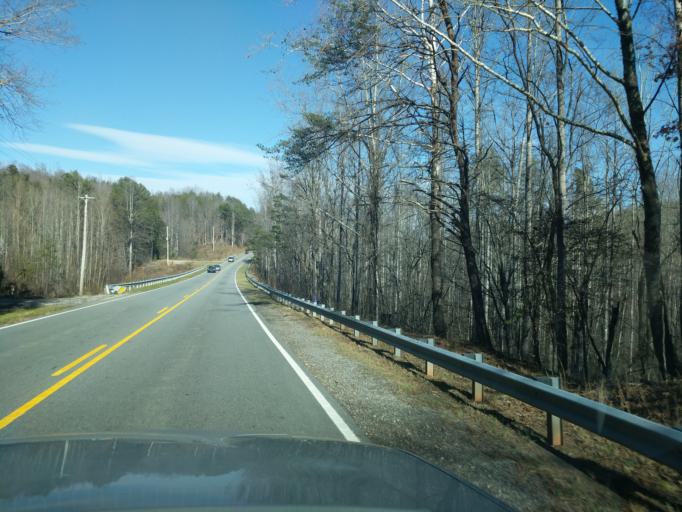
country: US
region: North Carolina
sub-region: McDowell County
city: West Marion
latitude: 35.5367
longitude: -81.9661
